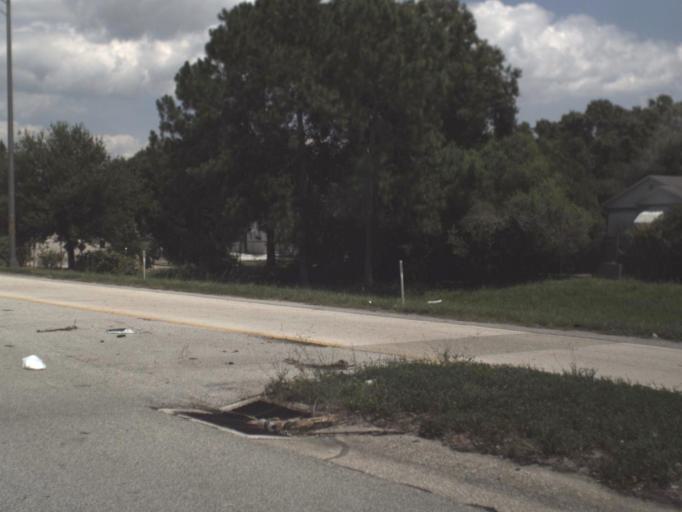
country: US
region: Florida
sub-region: Pinellas County
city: Lealman
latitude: 27.8096
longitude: -82.6632
